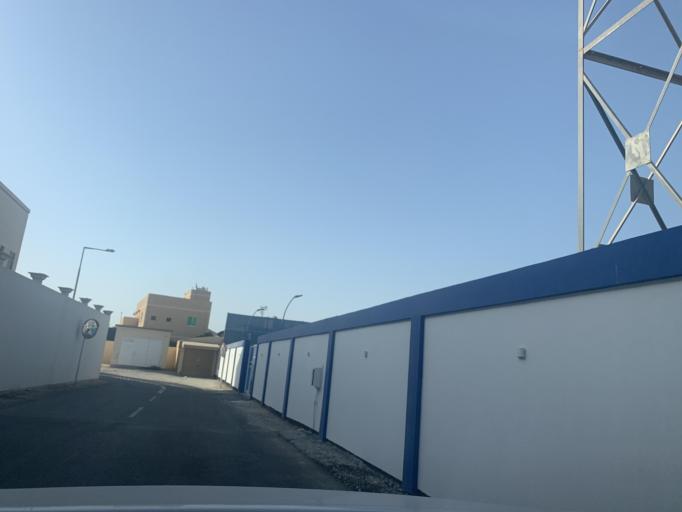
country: BH
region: Manama
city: Jidd Hafs
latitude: 26.1974
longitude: 50.4823
